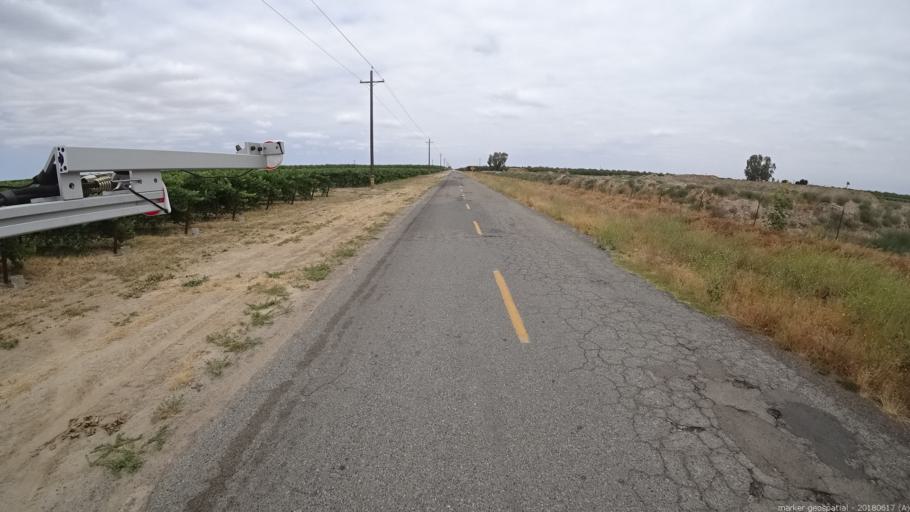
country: US
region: California
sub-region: Madera County
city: Parkwood
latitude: 36.8485
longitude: -120.1647
